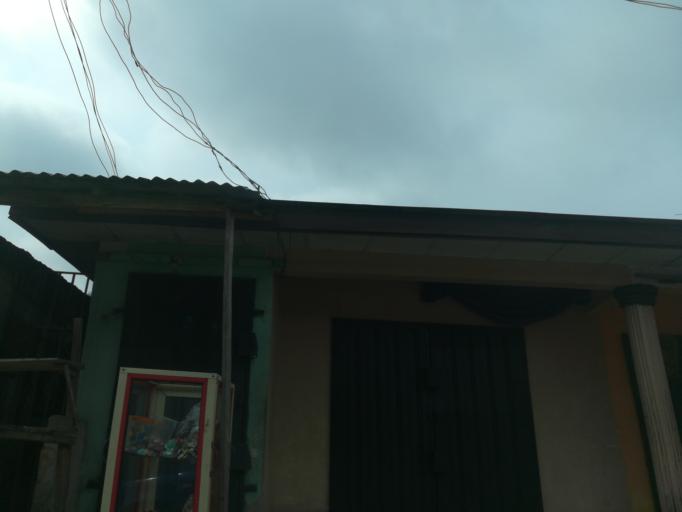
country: NG
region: Rivers
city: Port Harcourt
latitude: 4.8712
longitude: 6.9864
